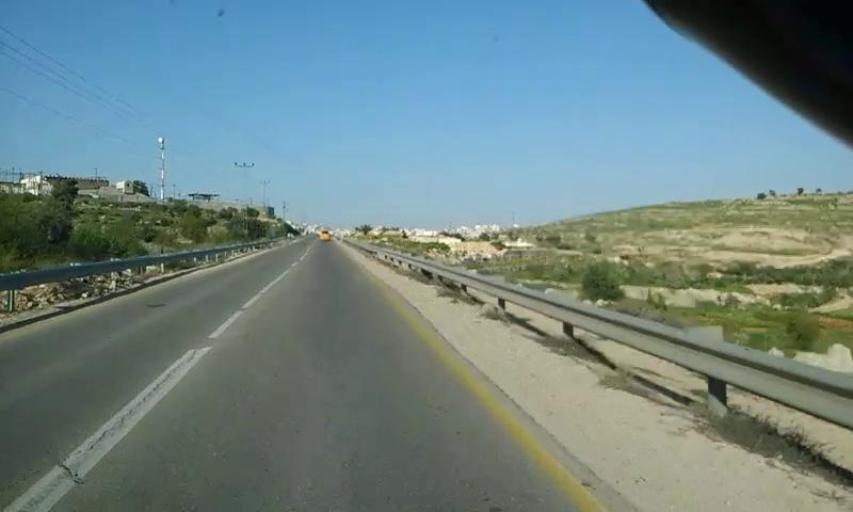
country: PS
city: Khallat ad Dar
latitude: 31.5004
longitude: 35.1053
